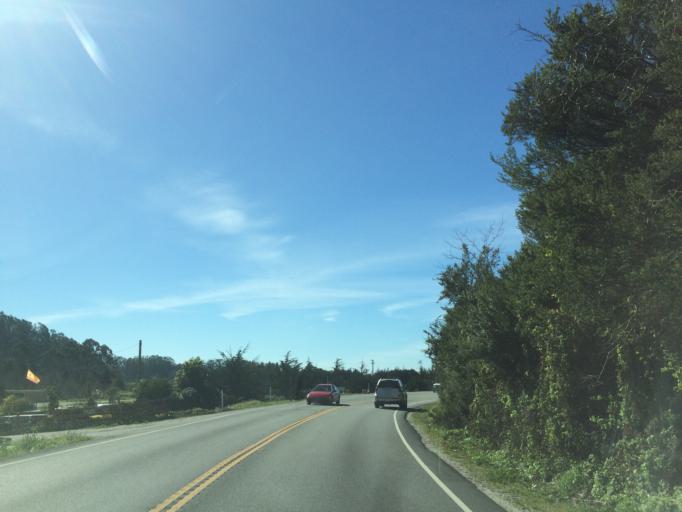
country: US
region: California
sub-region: San Mateo County
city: Half Moon Bay
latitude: 37.4709
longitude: -122.4223
